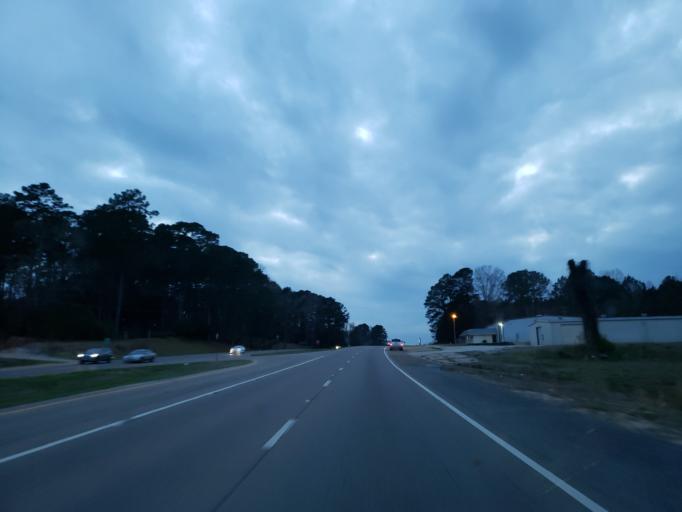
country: US
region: Mississippi
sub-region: Lauderdale County
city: Marion
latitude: 32.3672
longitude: -88.6416
